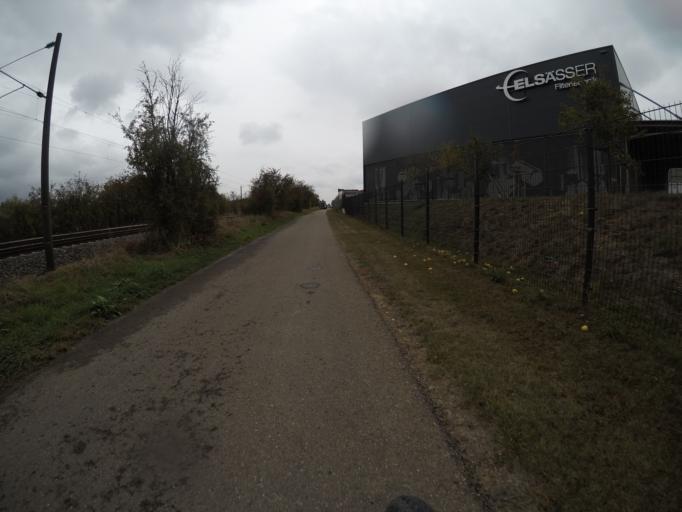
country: DE
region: Baden-Wuerttemberg
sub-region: Regierungsbezirk Stuttgart
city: Gartringen
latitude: 48.6327
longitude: 8.9028
